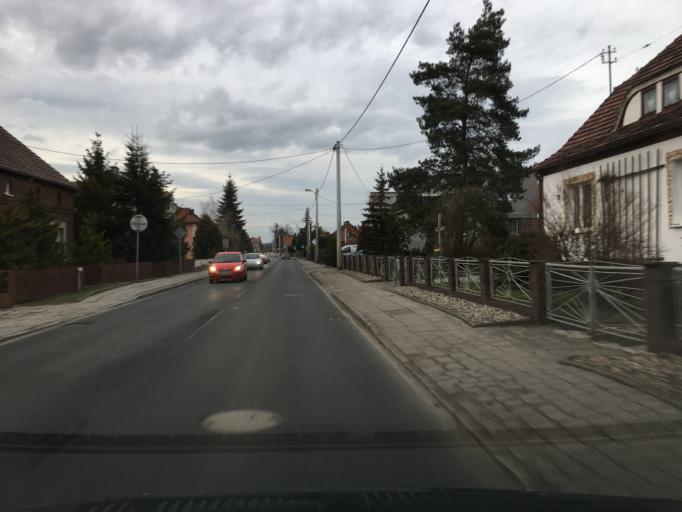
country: PL
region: Opole Voivodeship
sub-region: Powiat kedzierzynsko-kozielski
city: Kozle
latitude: 50.3537
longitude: 18.1656
